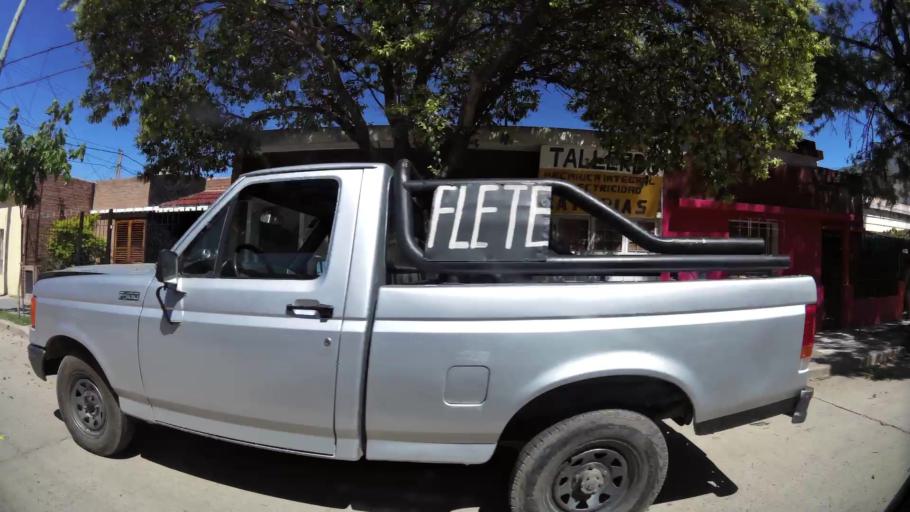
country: AR
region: Cordoba
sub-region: Departamento de Capital
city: Cordoba
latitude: -31.4155
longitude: -64.1368
